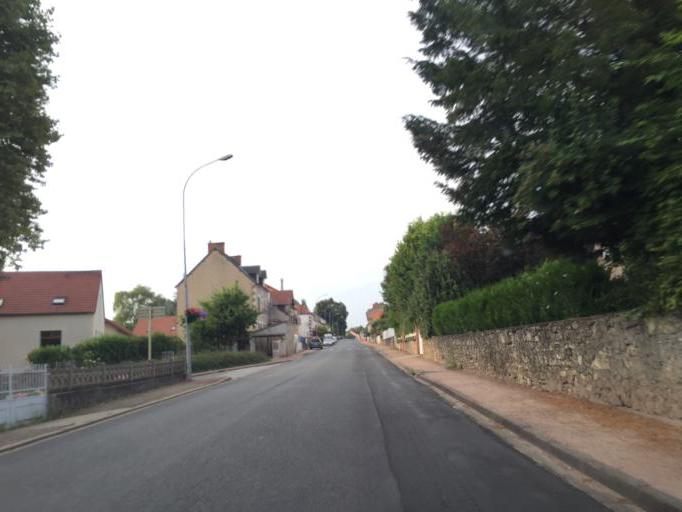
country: FR
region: Auvergne
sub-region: Departement de l'Allier
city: Saint-Germain-des-Fosses
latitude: 46.2100
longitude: 3.4325
